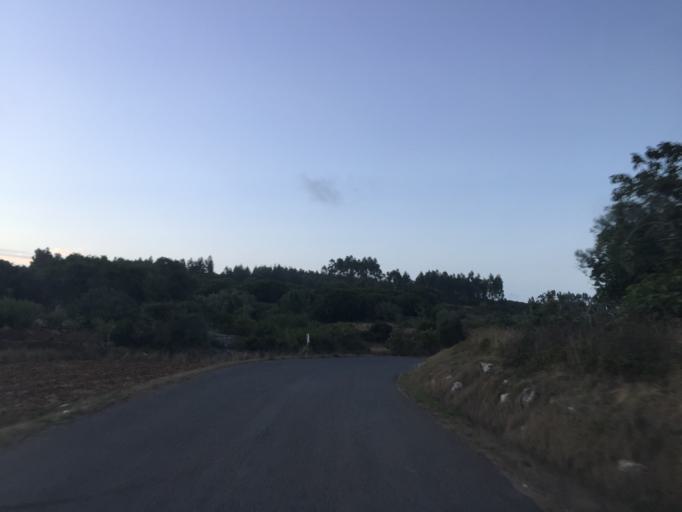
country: PT
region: Leiria
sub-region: Bombarral
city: Bombarral
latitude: 39.2926
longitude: -9.2072
